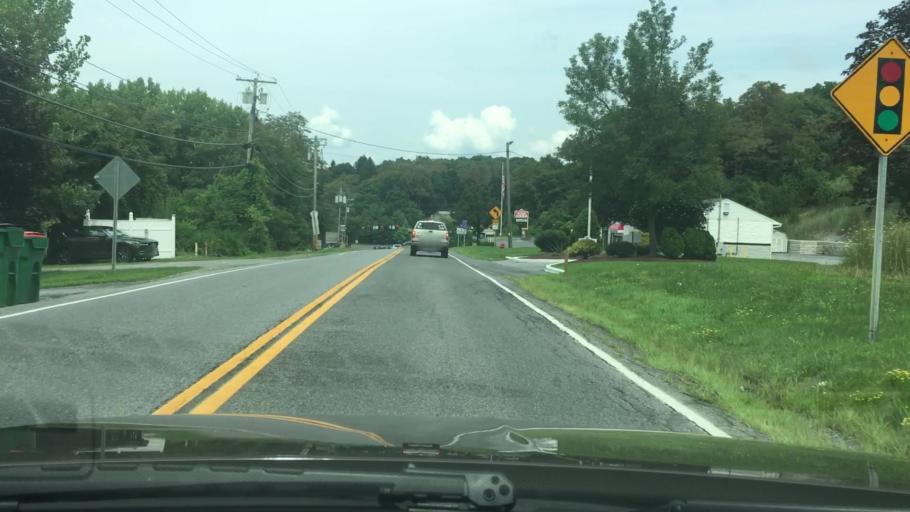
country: US
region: New York
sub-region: Dutchess County
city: Red Oaks Mill
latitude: 41.6576
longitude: -73.8474
